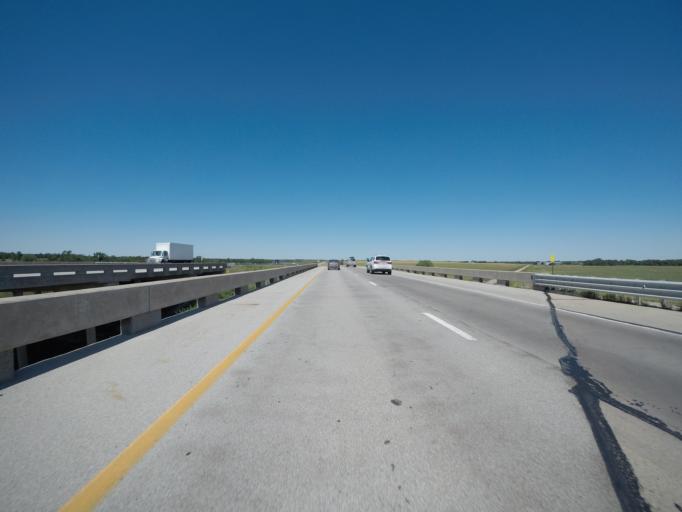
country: US
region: Kansas
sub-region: Saline County
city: Salina
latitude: 38.8782
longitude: -97.8077
